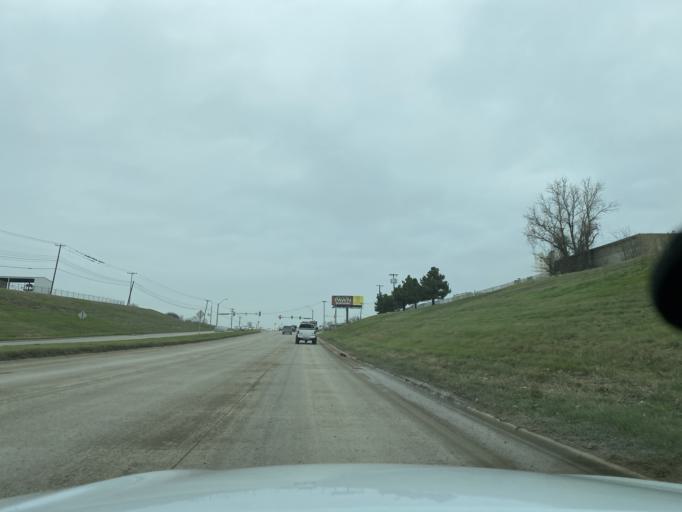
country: US
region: Texas
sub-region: Tarrant County
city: Euless
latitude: 32.8091
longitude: -97.0996
